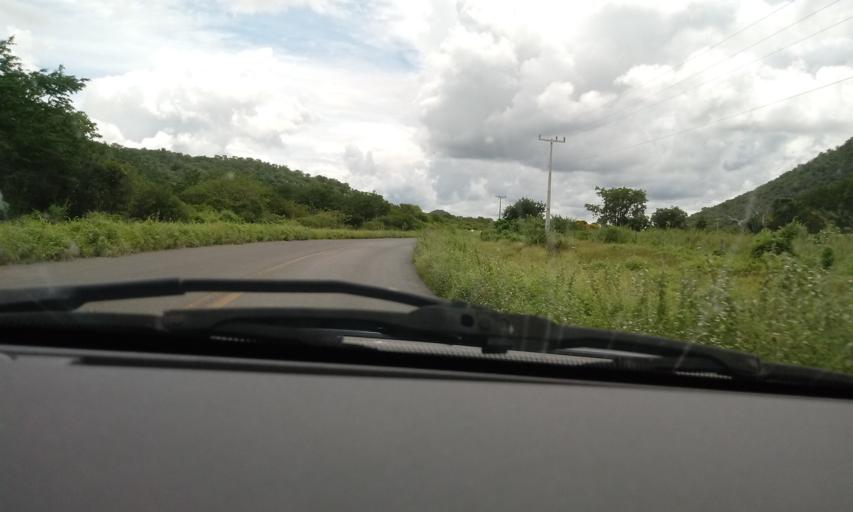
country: BR
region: Bahia
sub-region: Guanambi
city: Guanambi
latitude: -14.1460
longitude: -42.8410
